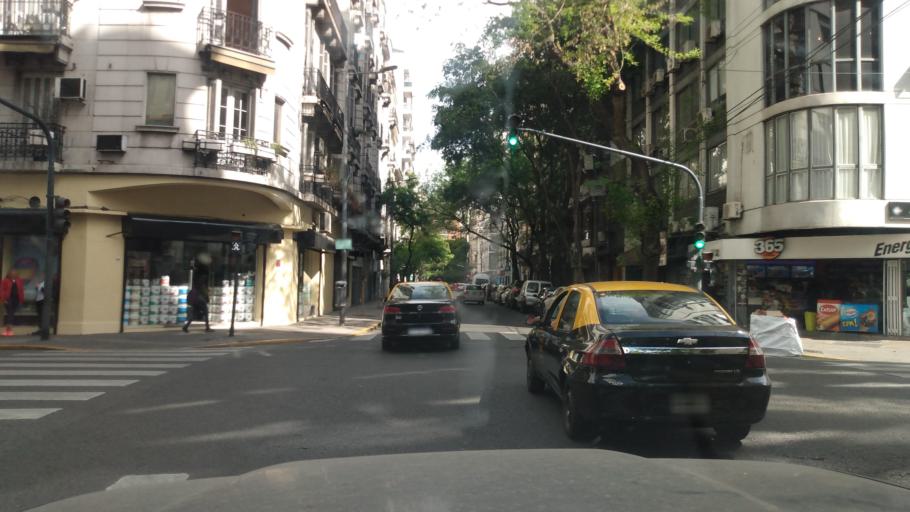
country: AR
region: Buenos Aires F.D.
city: Buenos Aires
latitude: -34.6006
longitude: -58.3914
